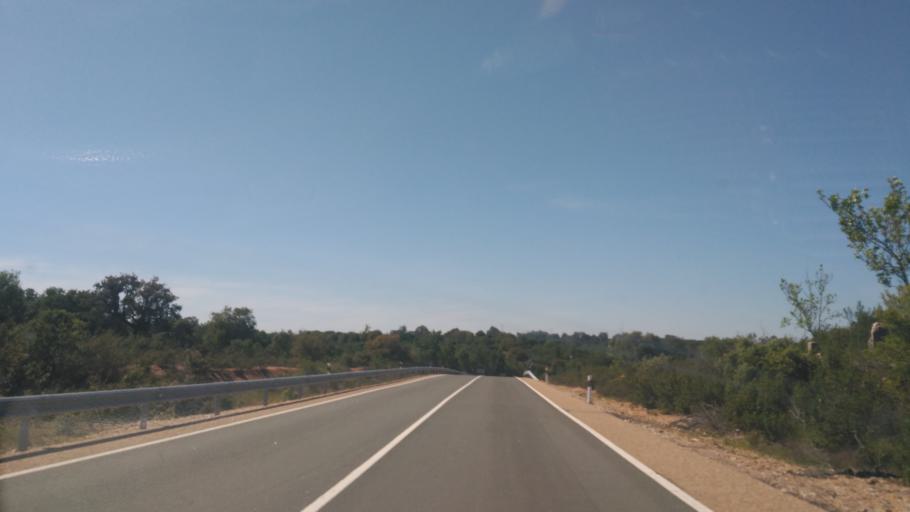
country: ES
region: Castille and Leon
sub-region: Provincia de Zamora
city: Cuelgamures
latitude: 41.2870
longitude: -5.7221
